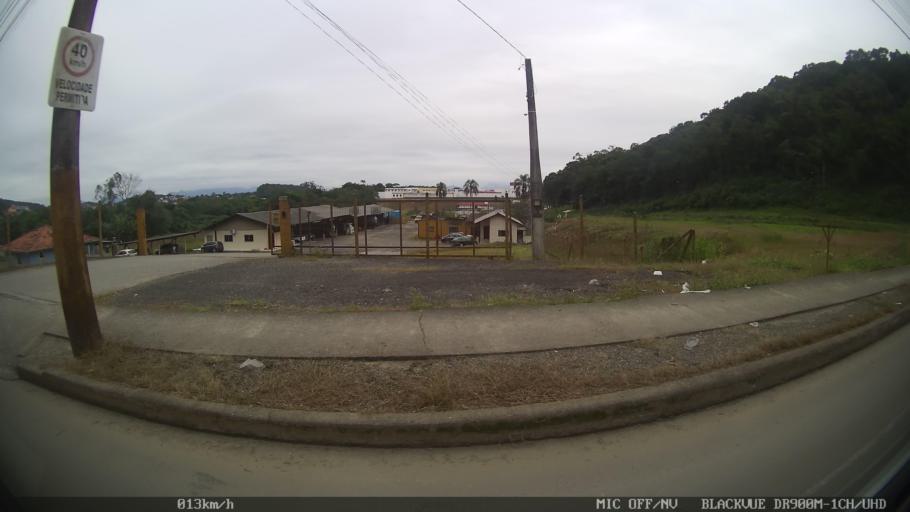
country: BR
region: Santa Catarina
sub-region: Joinville
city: Joinville
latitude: -26.3580
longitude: -48.7994
